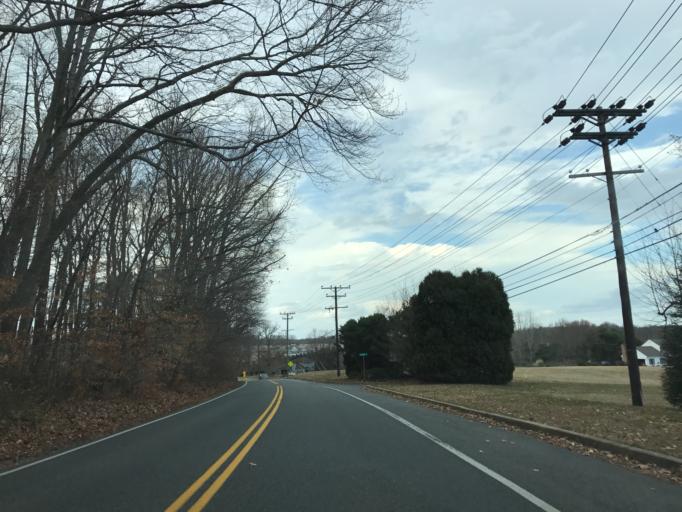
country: US
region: Maryland
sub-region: Harford County
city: Bel Air South
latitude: 39.5328
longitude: -76.2804
